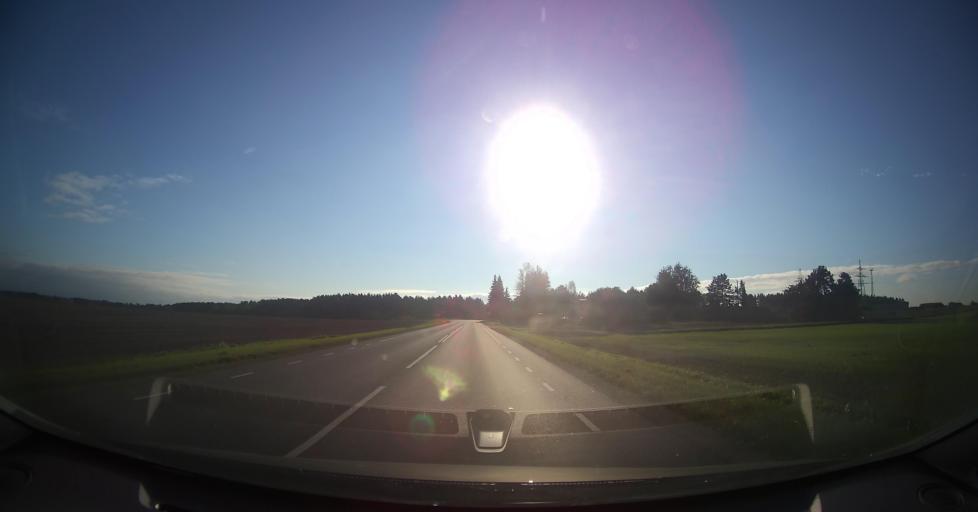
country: EE
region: Harju
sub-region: Raasiku vald
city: Arukula
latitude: 59.3642
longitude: 25.0479
